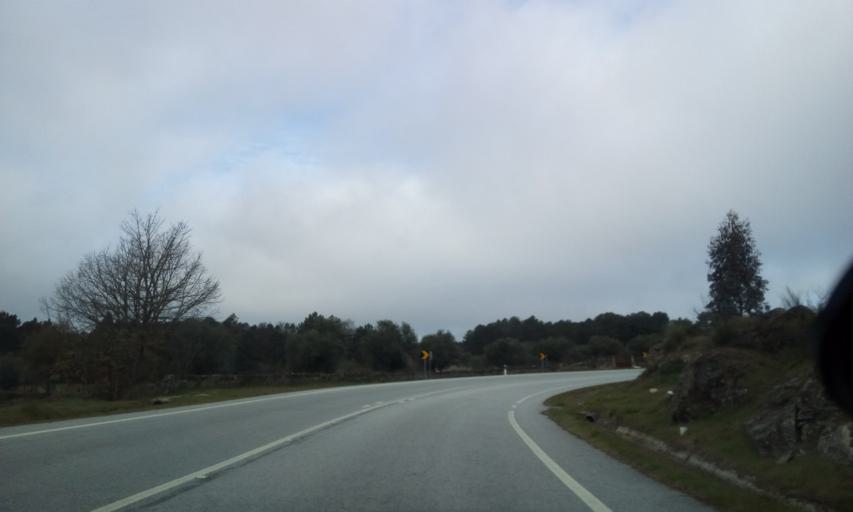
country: PT
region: Guarda
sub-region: Fornos de Algodres
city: Fornos de Algodres
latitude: 40.7196
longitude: -7.4900
